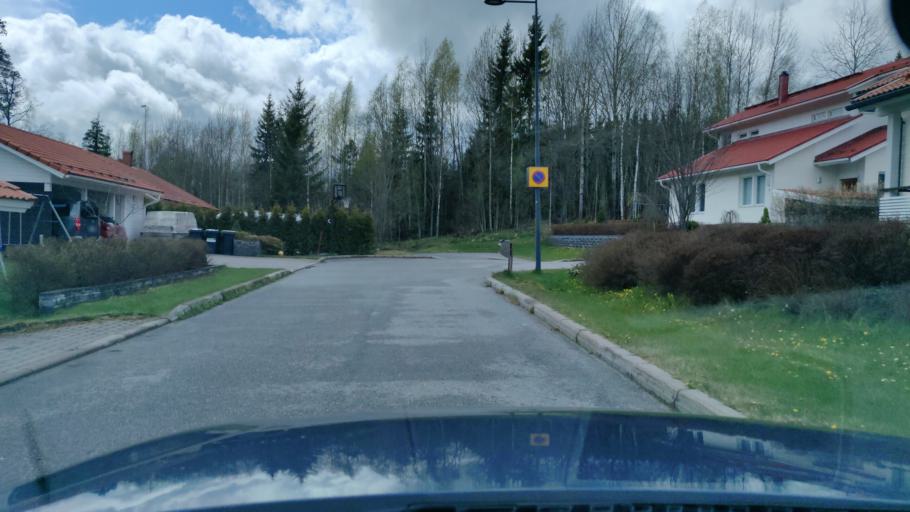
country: FI
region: Uusimaa
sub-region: Helsinki
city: Nurmijaervi
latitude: 60.3609
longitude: 24.7262
